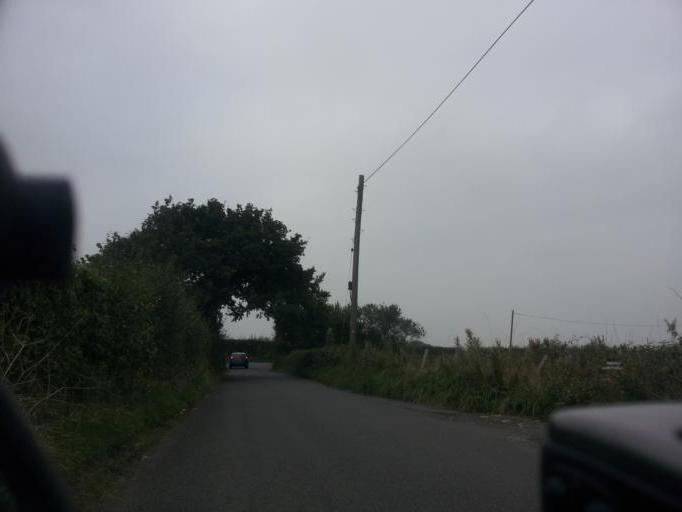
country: GB
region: England
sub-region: Kent
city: Newington
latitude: 51.3676
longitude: 0.6955
